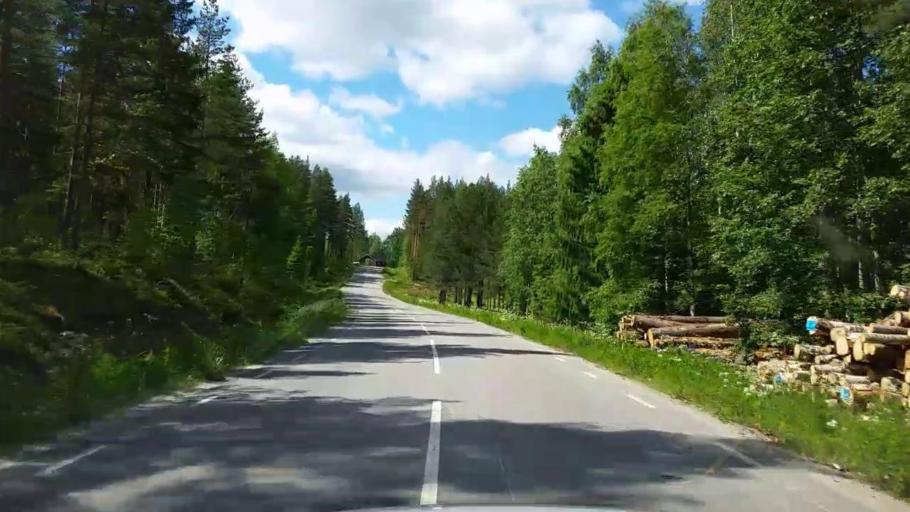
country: SE
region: Gaevleborg
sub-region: Ovanakers Kommun
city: Alfta
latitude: 61.2563
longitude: 16.1315
